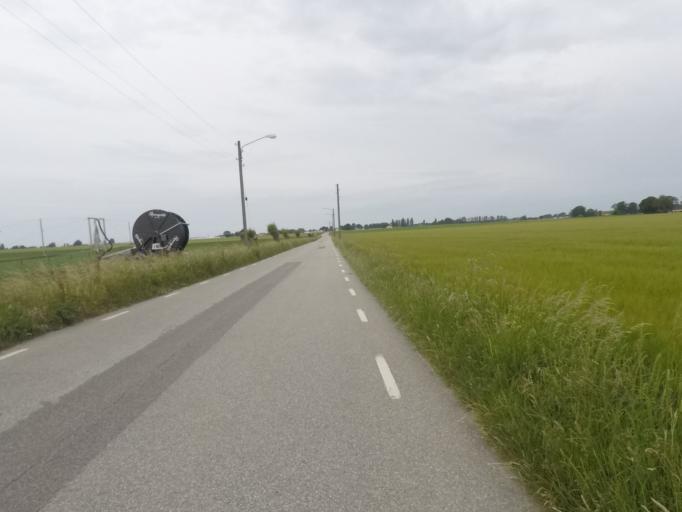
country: SE
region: Skane
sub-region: Malmo
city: Bunkeflostrand
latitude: 55.5131
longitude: 12.9675
